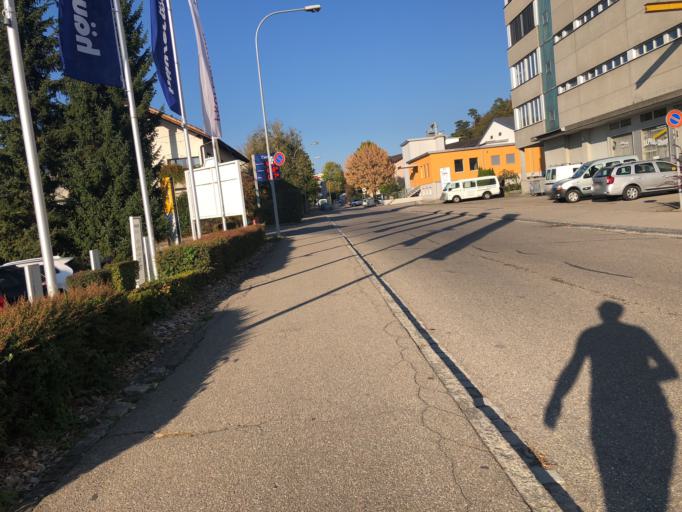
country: CH
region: Zurich
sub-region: Bezirk Pfaeffikon
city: Effretikon
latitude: 47.4206
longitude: 8.6831
